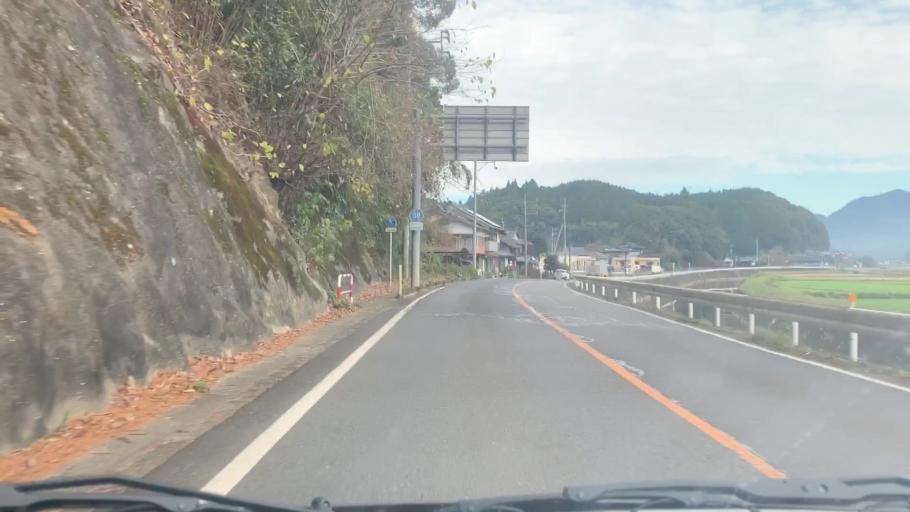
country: JP
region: Saga Prefecture
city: Takeocho-takeo
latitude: 33.2278
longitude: 129.9638
